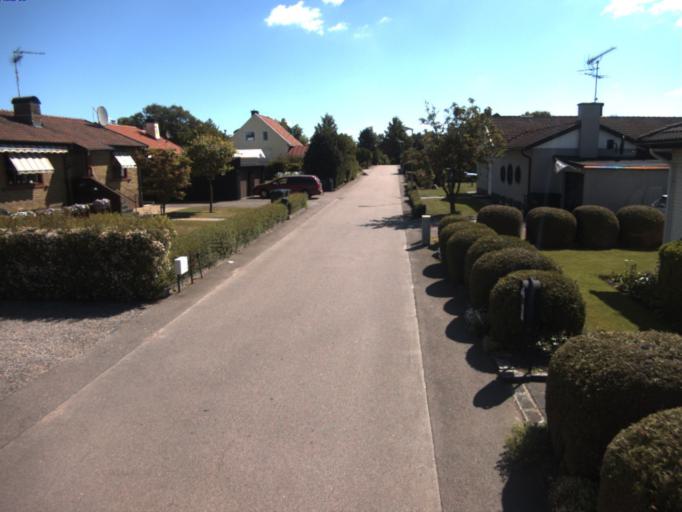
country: SE
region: Skane
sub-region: Helsingborg
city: Barslov
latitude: 56.0046
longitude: 12.8183
